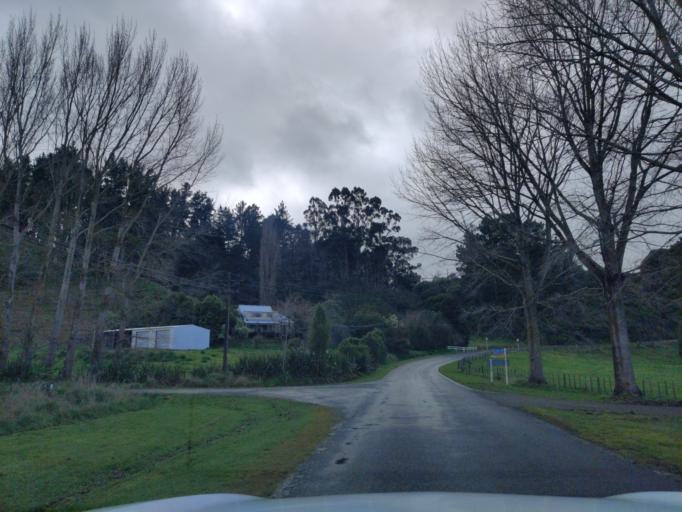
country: NZ
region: Manawatu-Wanganui
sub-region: Palmerston North City
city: Palmerston North
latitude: -40.1680
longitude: 175.8022
